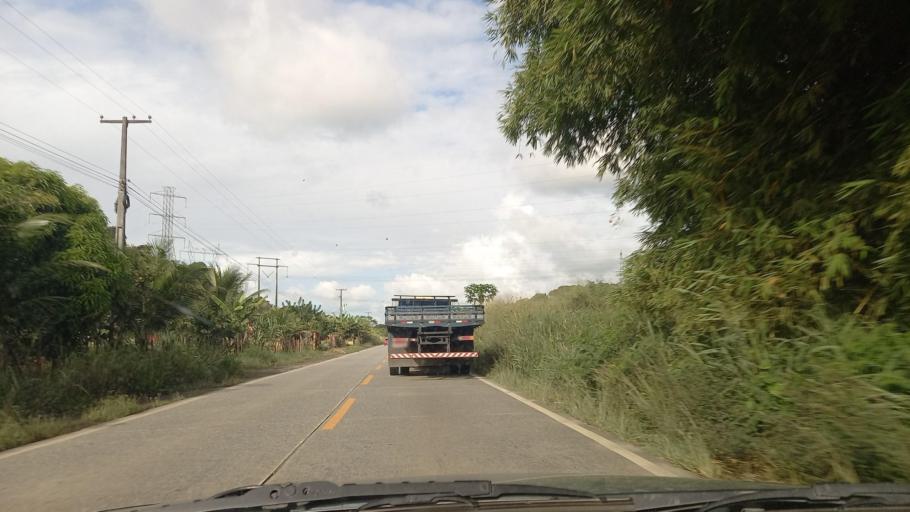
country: BR
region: Pernambuco
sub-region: Palmares
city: Palmares
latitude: -8.6913
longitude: -35.6180
